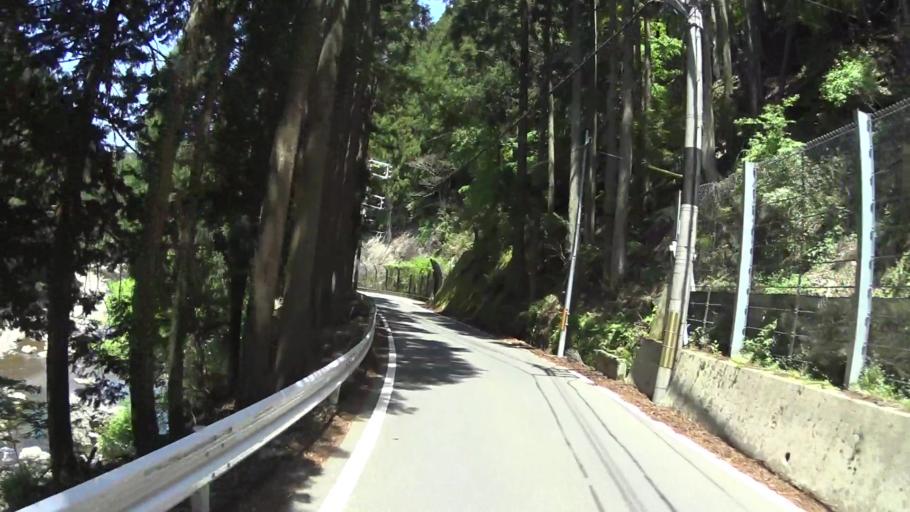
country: JP
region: Shiga Prefecture
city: Kitahama
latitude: 35.2061
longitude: 135.7590
